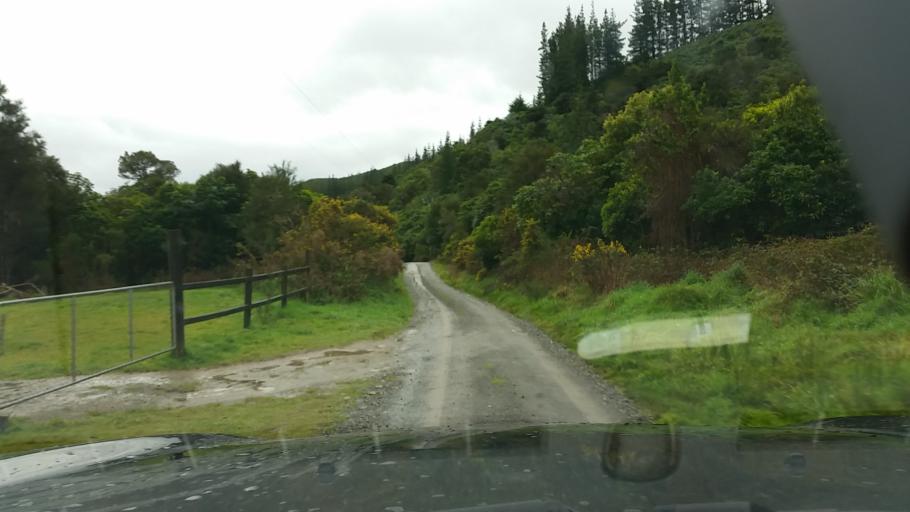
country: NZ
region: Marlborough
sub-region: Marlborough District
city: Picton
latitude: -41.2914
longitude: 174.0404
